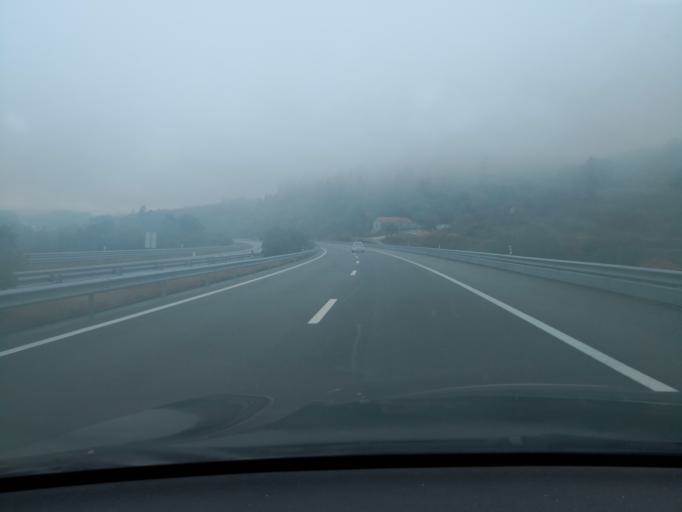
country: PT
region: Braga
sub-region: Celorico de Basto
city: Celorico de Basto
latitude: 41.4471
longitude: -8.0588
